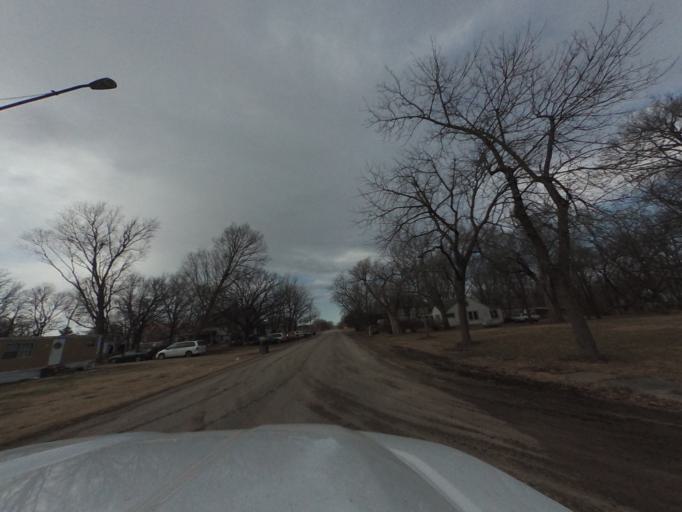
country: US
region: Kansas
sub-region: Chase County
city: Cottonwood Falls
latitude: 38.3735
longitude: -96.6439
